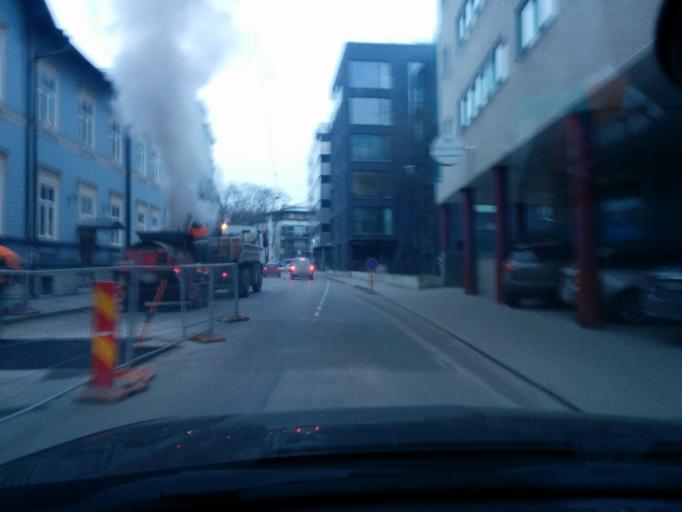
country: EE
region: Harju
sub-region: Tallinna linn
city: Tallinn
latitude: 59.4376
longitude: 24.7738
